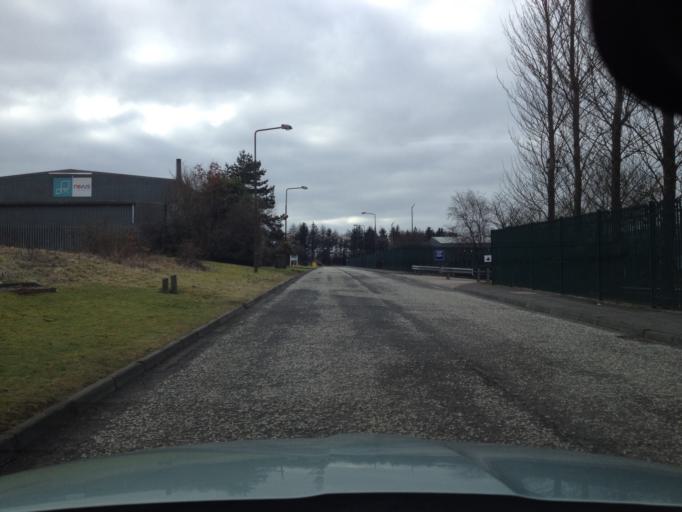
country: GB
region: Scotland
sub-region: West Lothian
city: Livingston
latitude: 55.9138
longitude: -3.5163
